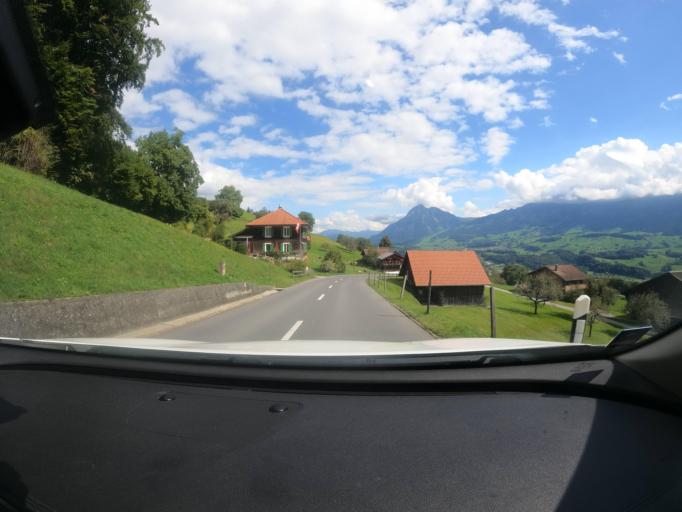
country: CH
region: Obwalden
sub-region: Obwalden
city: Sachseln
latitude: 46.8906
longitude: 8.2234
